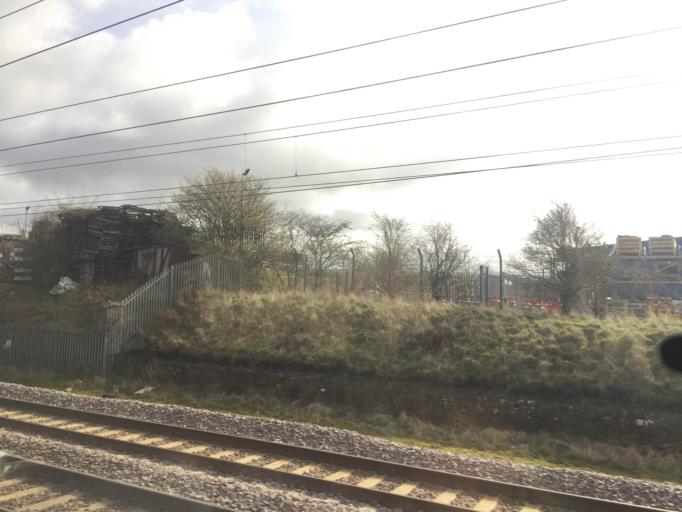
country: GB
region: England
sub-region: Cumbria
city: Penrith
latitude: 54.6571
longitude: -2.7638
